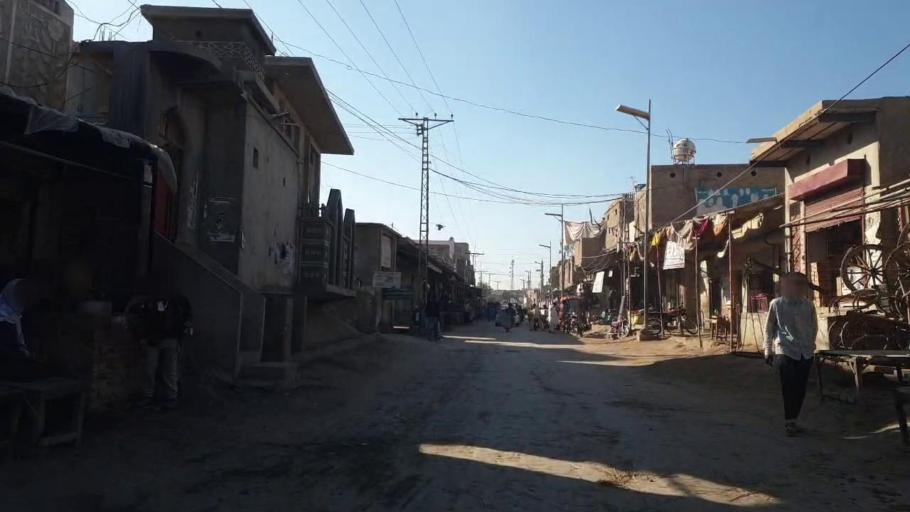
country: PK
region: Sindh
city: New Badah
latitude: 27.3287
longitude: 68.0246
